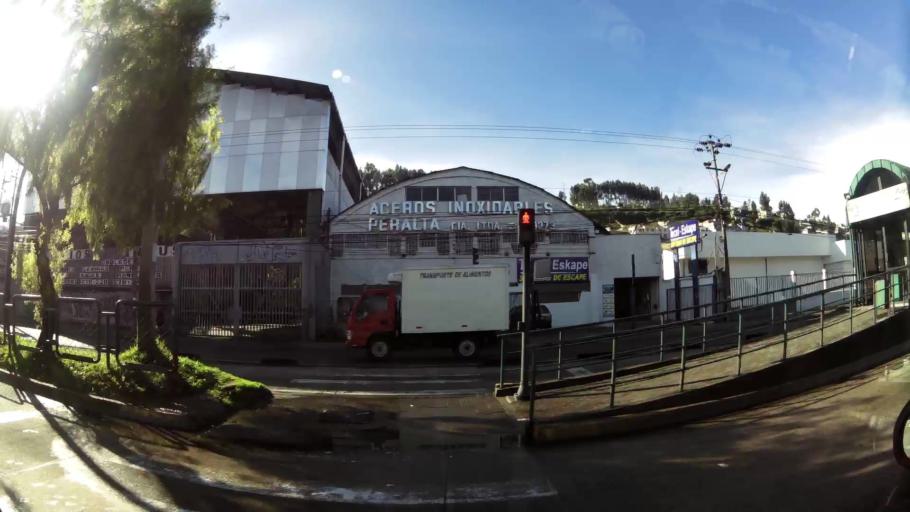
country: EC
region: Pichincha
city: Quito
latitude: -0.2784
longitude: -78.5318
